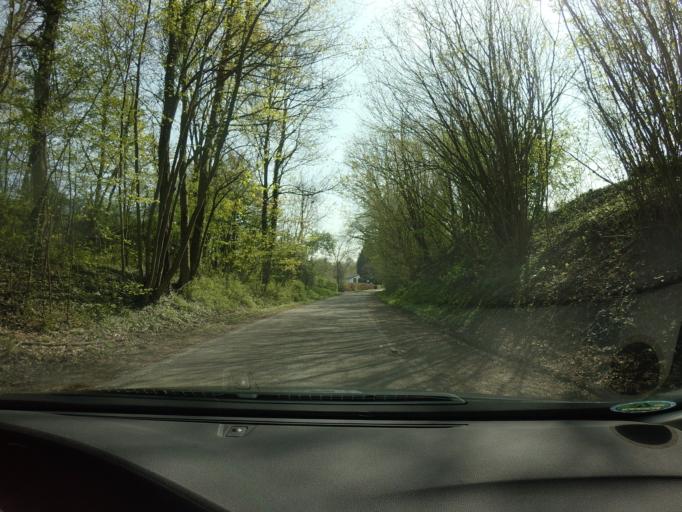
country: NL
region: Limburg
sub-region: Valkenburg aan de Geul
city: Berg
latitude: 50.8425
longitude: 5.7628
